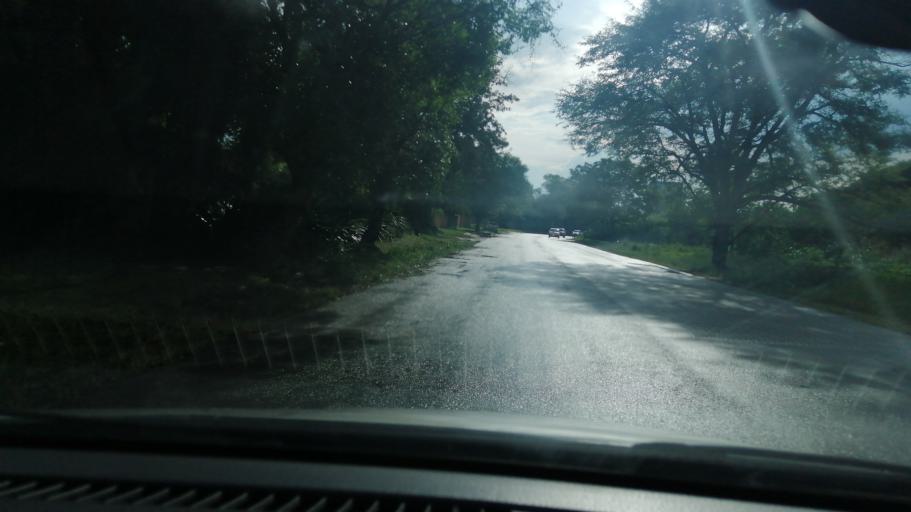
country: ZW
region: Harare
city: Harare
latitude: -17.7899
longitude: 31.0509
